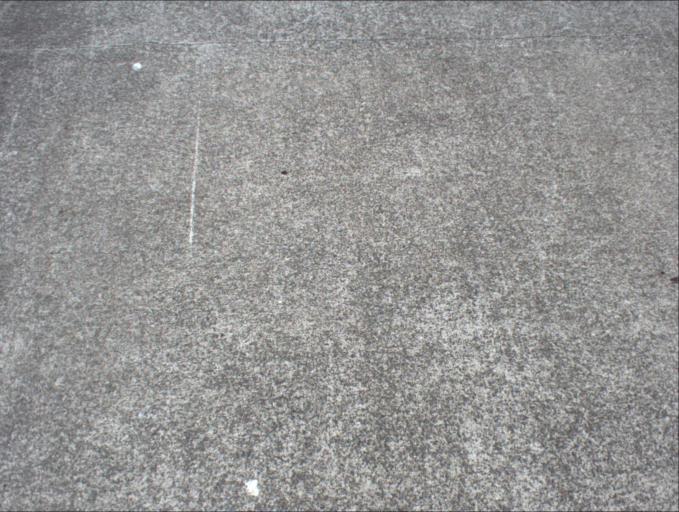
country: AU
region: Queensland
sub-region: Logan
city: Beenleigh
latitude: -27.6939
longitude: 153.1931
